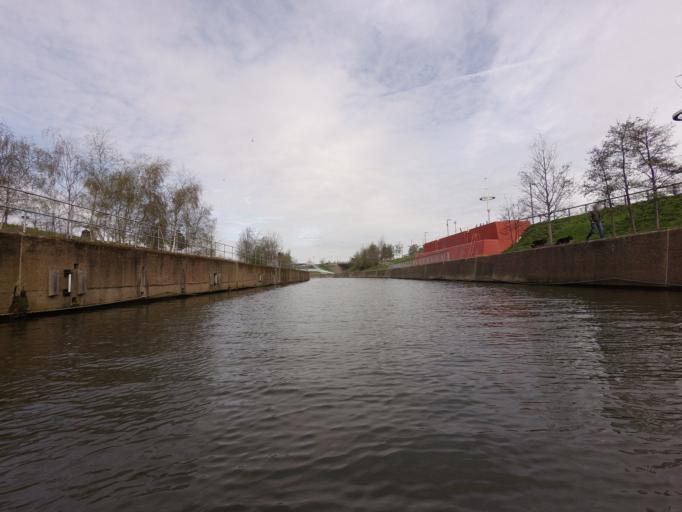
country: GB
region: England
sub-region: Greater London
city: Poplar
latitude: 51.5402
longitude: -0.0149
